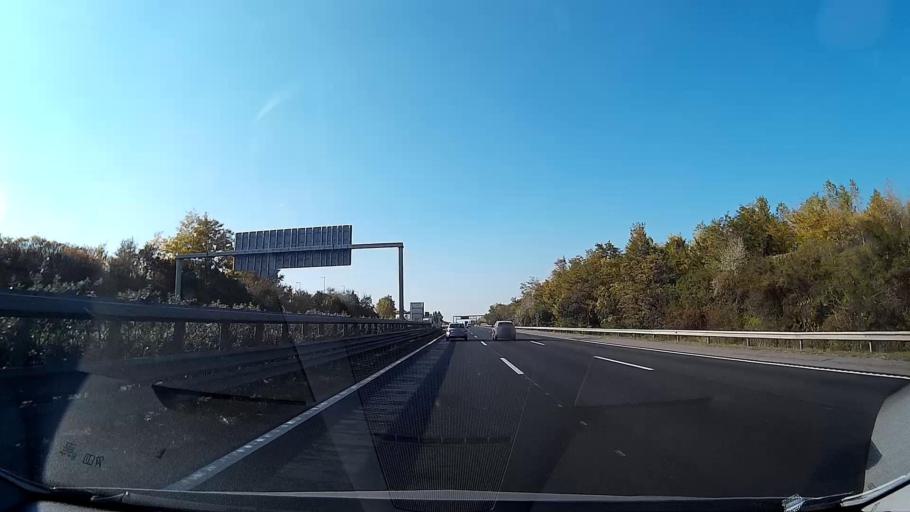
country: HU
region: Pest
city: Biatorbagy
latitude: 47.4705
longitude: 18.8610
